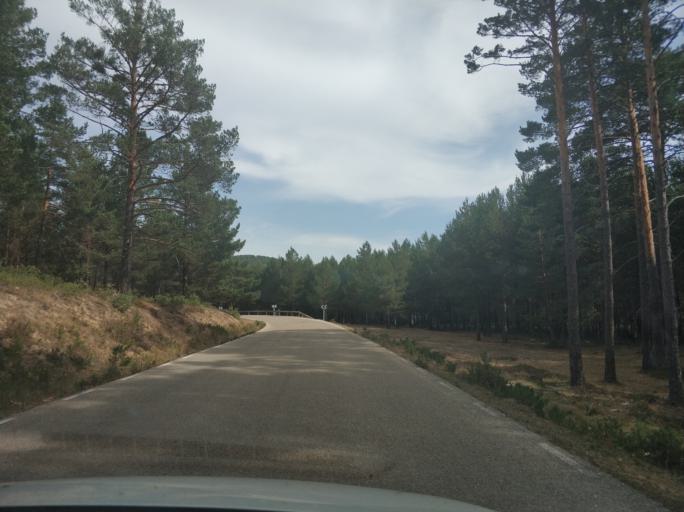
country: ES
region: Castille and Leon
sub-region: Provincia de Soria
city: Navaleno
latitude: 41.8769
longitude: -2.9375
